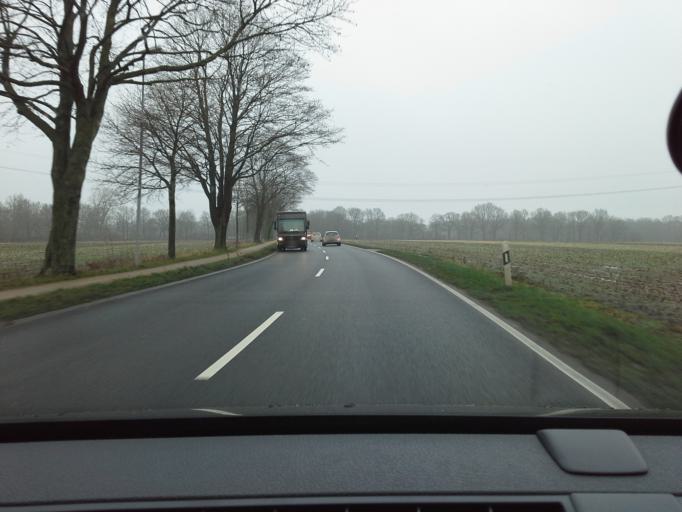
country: DE
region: Schleswig-Holstein
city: Ellerau
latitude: 53.7418
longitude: 9.9082
